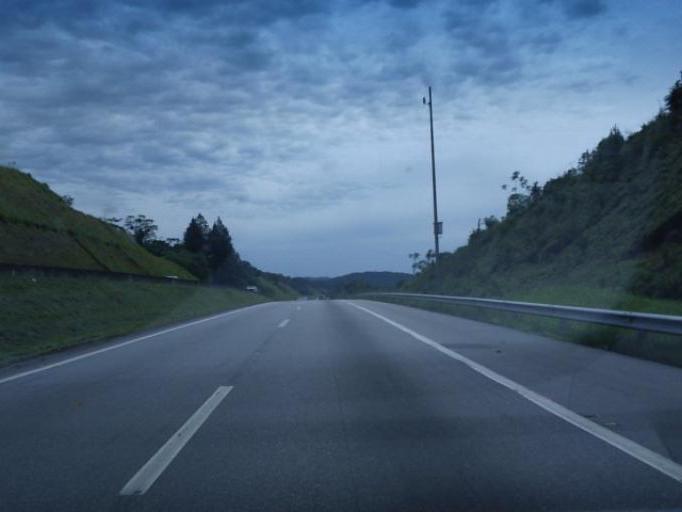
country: BR
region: Sao Paulo
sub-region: Miracatu
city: Miracatu
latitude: -24.1688
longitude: -47.3374
